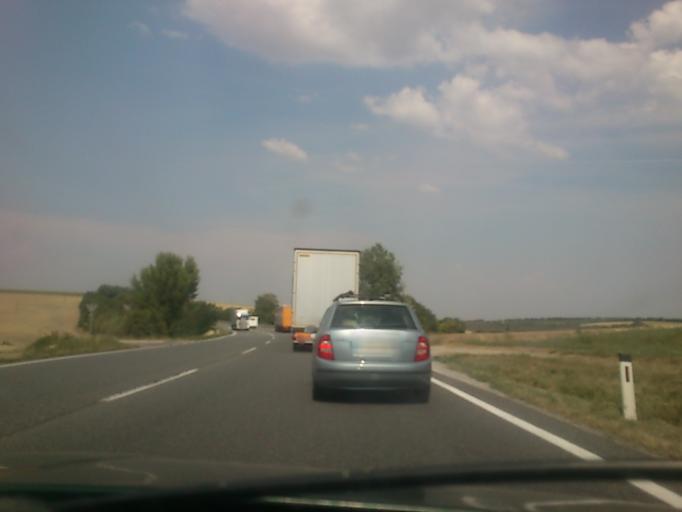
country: AT
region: Lower Austria
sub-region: Politischer Bezirk Mistelbach
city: Drasenhofen
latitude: 48.7275
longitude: 16.6578
